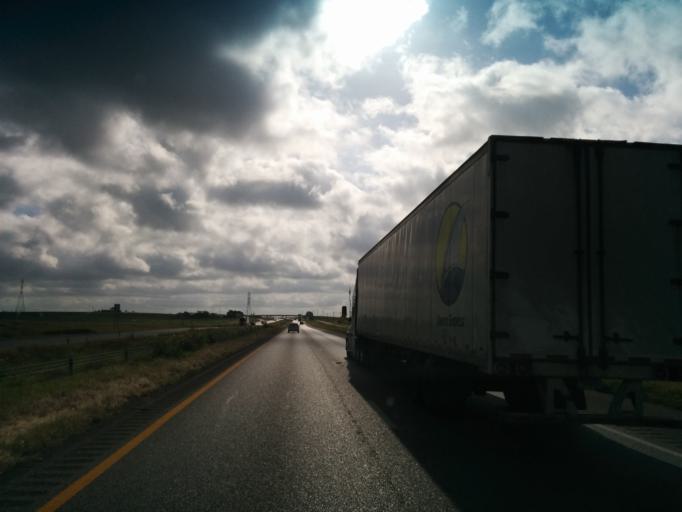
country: US
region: Texas
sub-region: Guadalupe County
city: Marion
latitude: 29.5336
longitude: -98.0947
